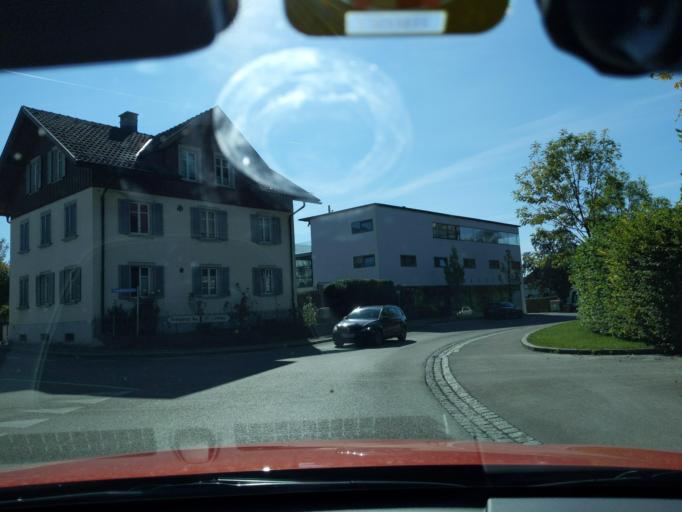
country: AT
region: Vorarlberg
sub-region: Politischer Bezirk Bregenz
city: Horbranz
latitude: 47.5550
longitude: 9.7504
